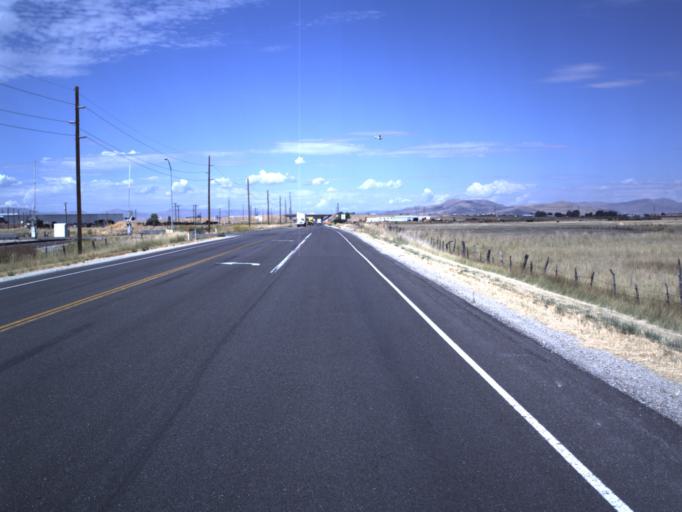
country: US
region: Utah
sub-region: Box Elder County
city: Brigham City
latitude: 41.5325
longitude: -112.0510
